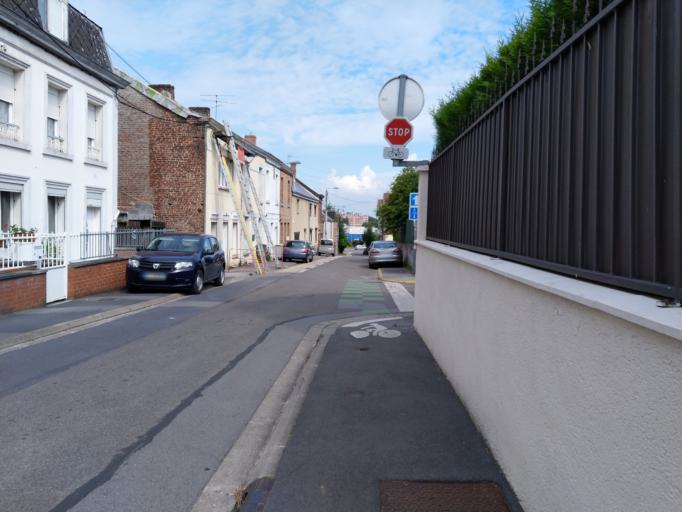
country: FR
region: Nord-Pas-de-Calais
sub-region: Departement du Nord
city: Maubeuge
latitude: 50.2697
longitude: 3.9741
